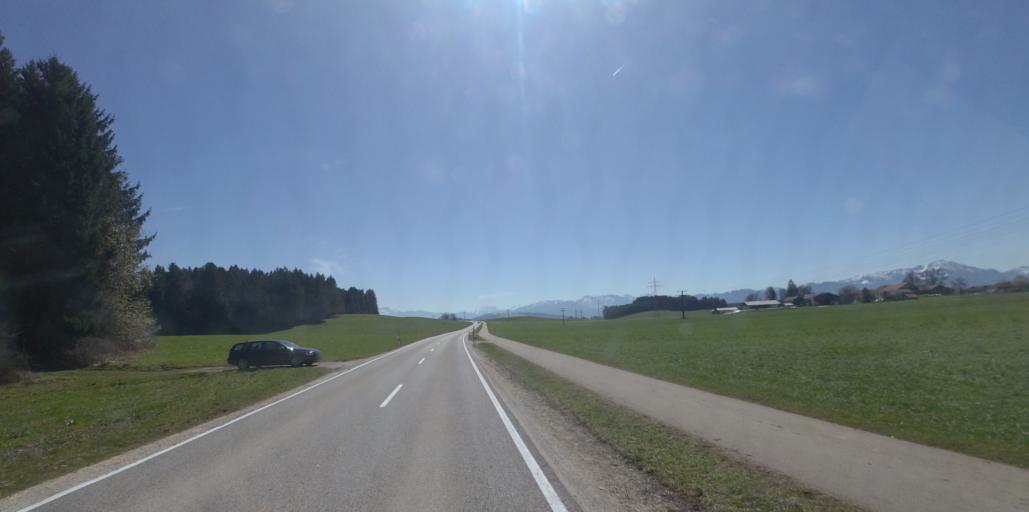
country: DE
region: Bavaria
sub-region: Upper Bavaria
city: Nussdorf
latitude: 47.8922
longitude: 12.6110
